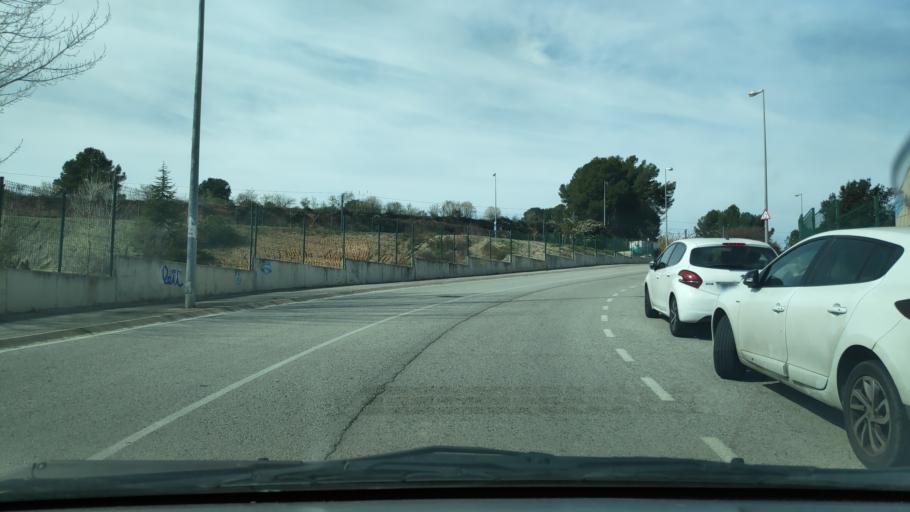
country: ES
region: Catalonia
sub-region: Provincia de Barcelona
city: Rubi
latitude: 41.5047
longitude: 2.0317
